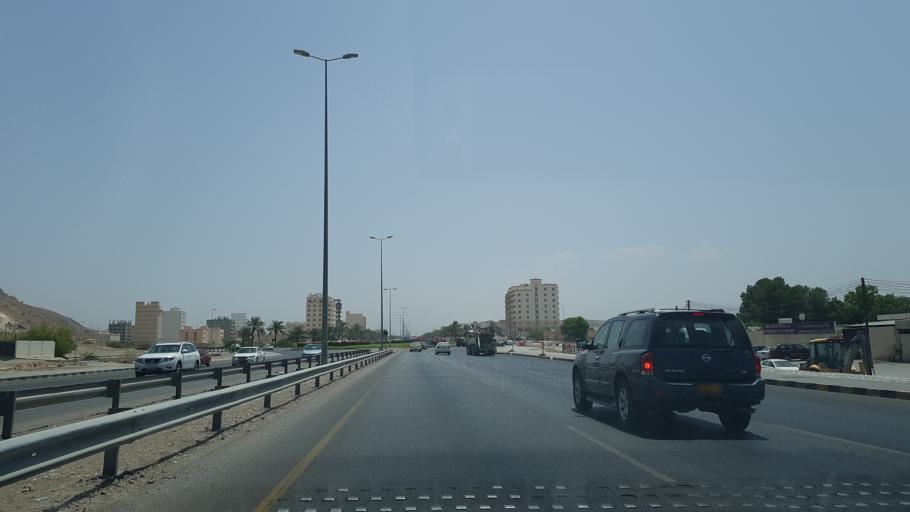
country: OM
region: Muhafazat Masqat
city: Muscat
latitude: 23.5365
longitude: 58.5125
